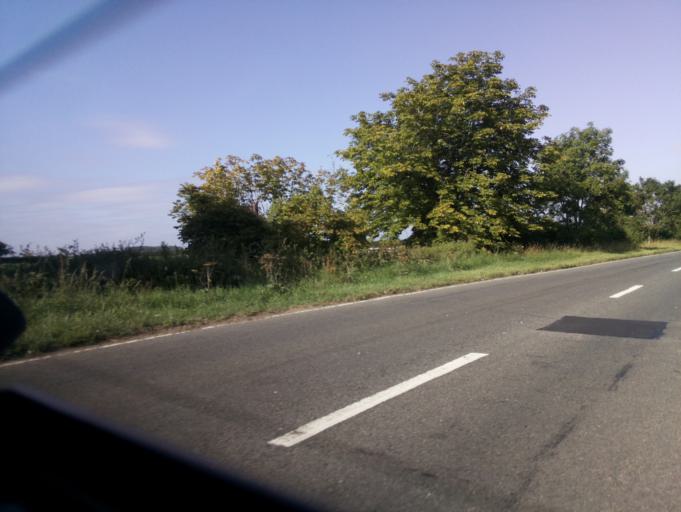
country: GB
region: England
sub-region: Oxfordshire
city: Bampton
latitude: 51.7230
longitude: -1.5598
